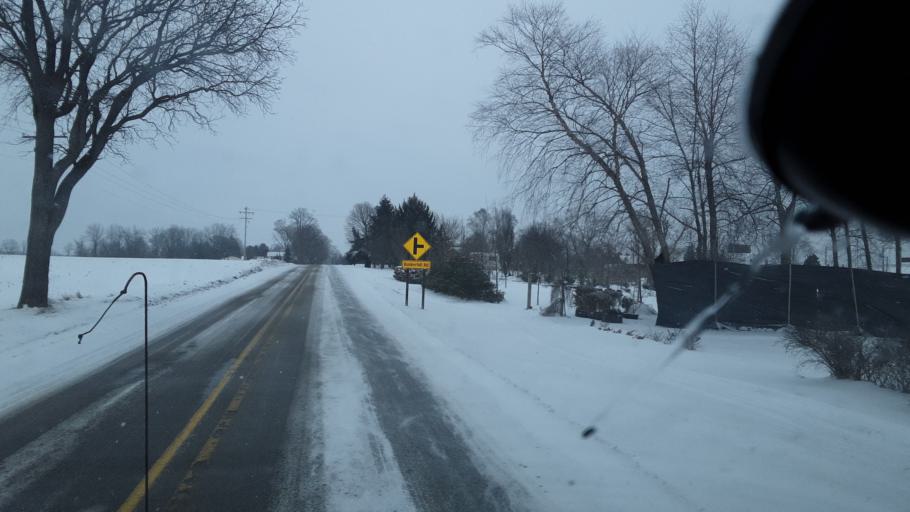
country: US
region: Michigan
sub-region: Ingham County
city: Leslie
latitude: 42.4247
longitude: -84.3149
